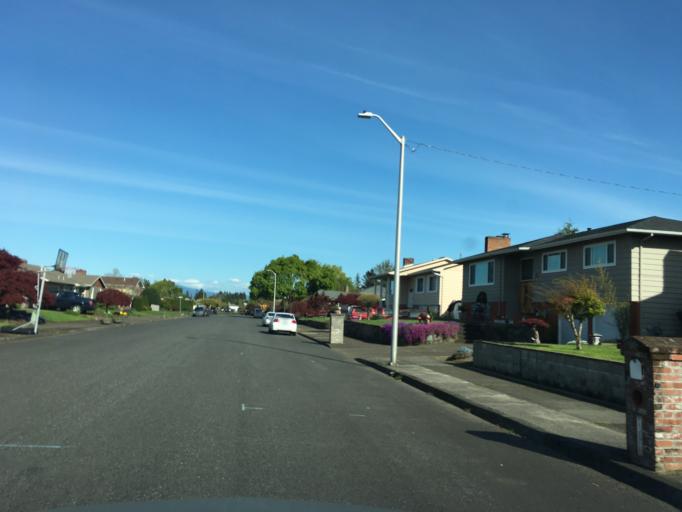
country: US
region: Oregon
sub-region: Multnomah County
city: Lents
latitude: 45.5447
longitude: -122.5205
